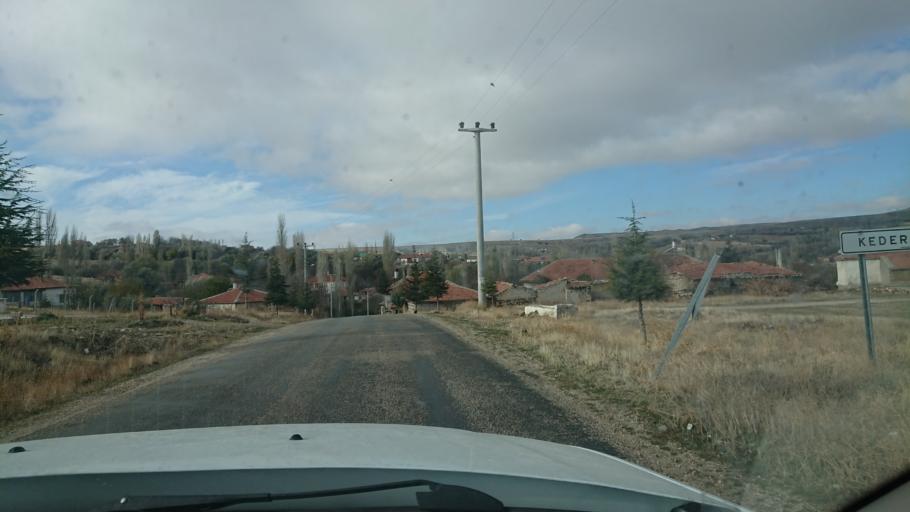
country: TR
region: Aksaray
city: Agacoren
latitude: 38.8188
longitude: 33.9622
